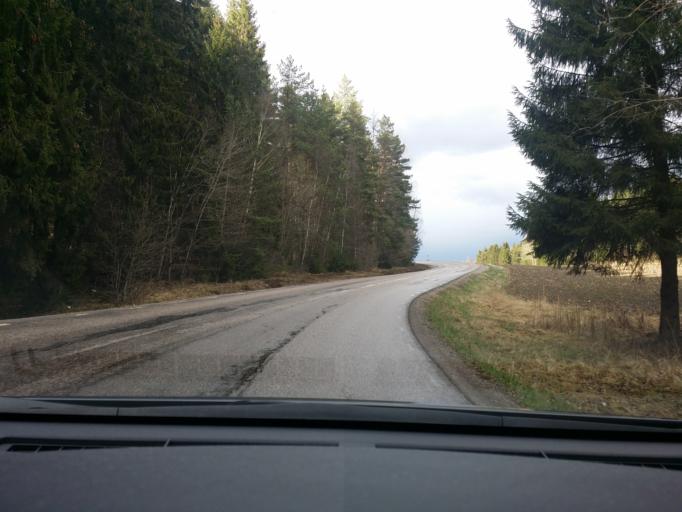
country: SE
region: Soedermanland
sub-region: Eskilstuna Kommun
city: Arla
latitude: 59.3137
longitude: 16.6804
